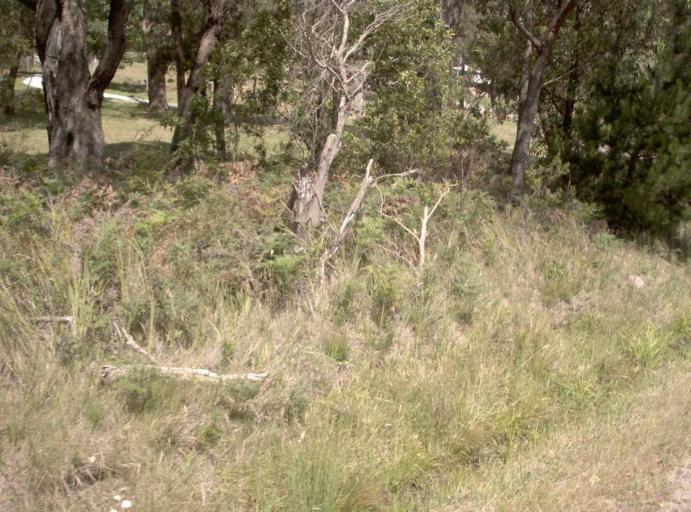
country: AU
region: Victoria
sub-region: Latrobe
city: Traralgon
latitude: -38.2995
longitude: 146.5383
